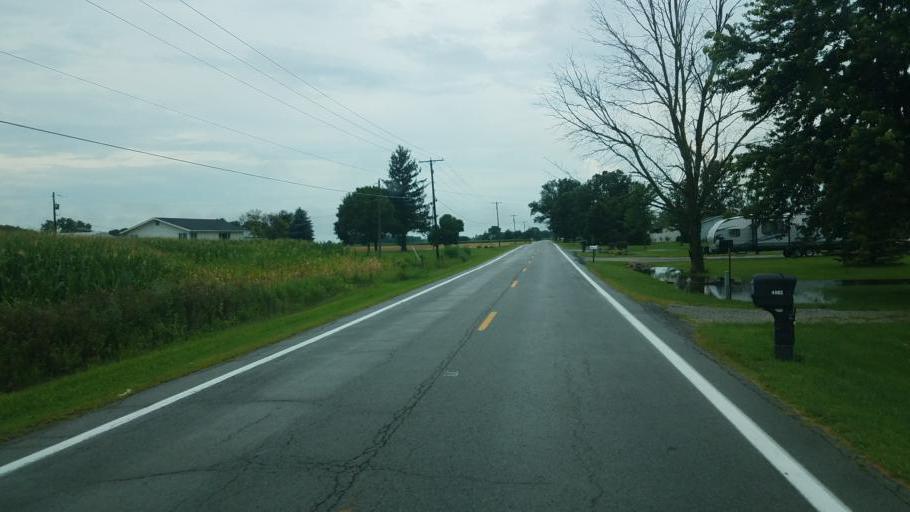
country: US
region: Ohio
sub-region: Marion County
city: Prospect
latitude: 40.5187
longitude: -83.2380
